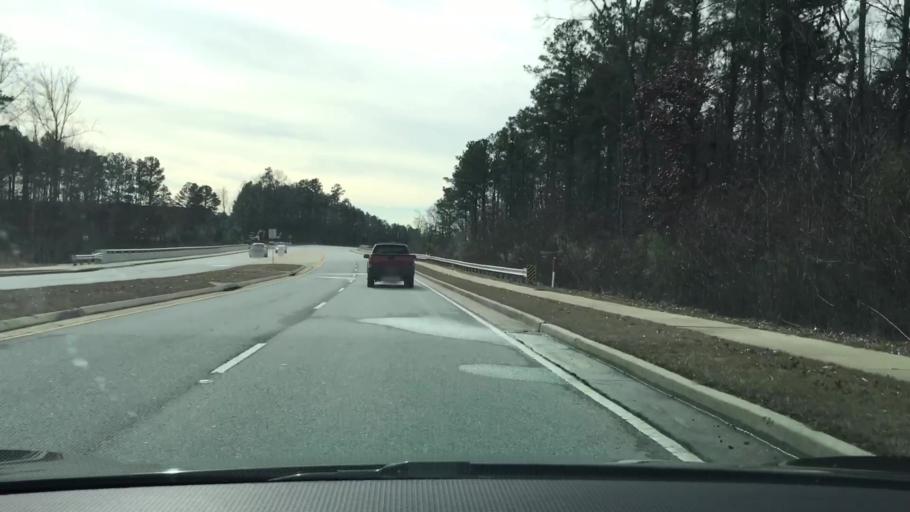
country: US
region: Georgia
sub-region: Gwinnett County
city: Suwanee
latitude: 34.0199
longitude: -84.0565
